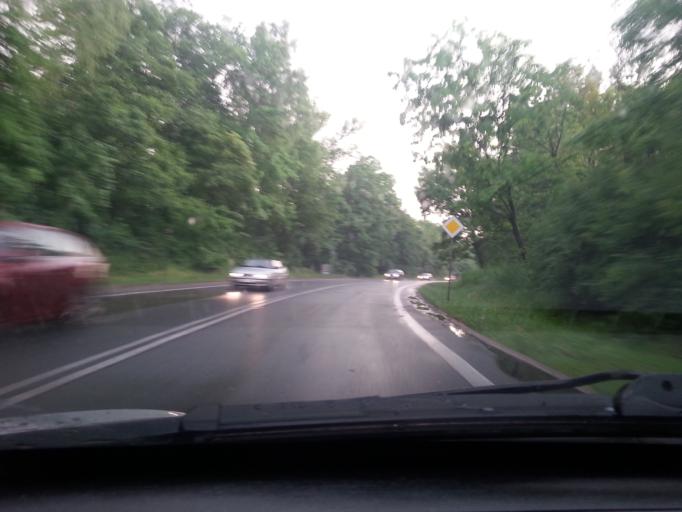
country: PL
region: Lodz Voivodeship
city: Lodz
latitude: 51.8082
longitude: 19.5013
